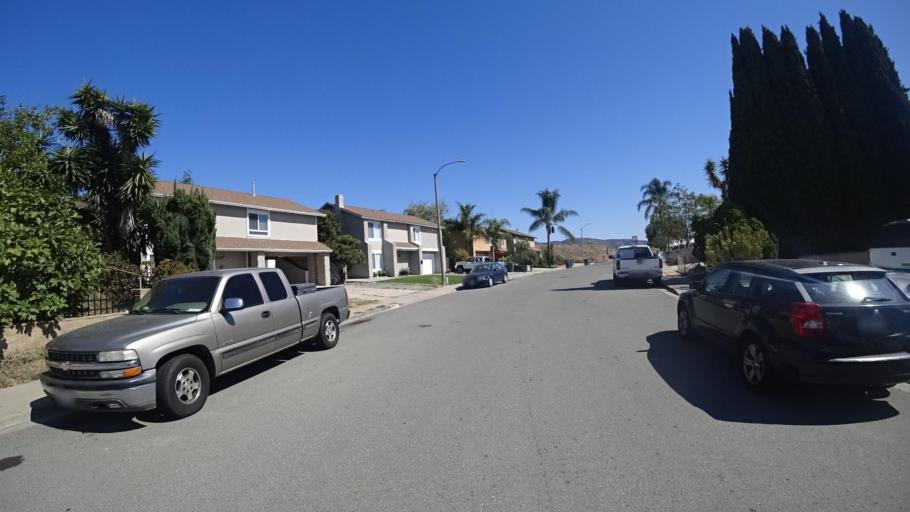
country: US
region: California
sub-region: San Diego County
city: La Presa
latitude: 32.6951
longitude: -117.0166
